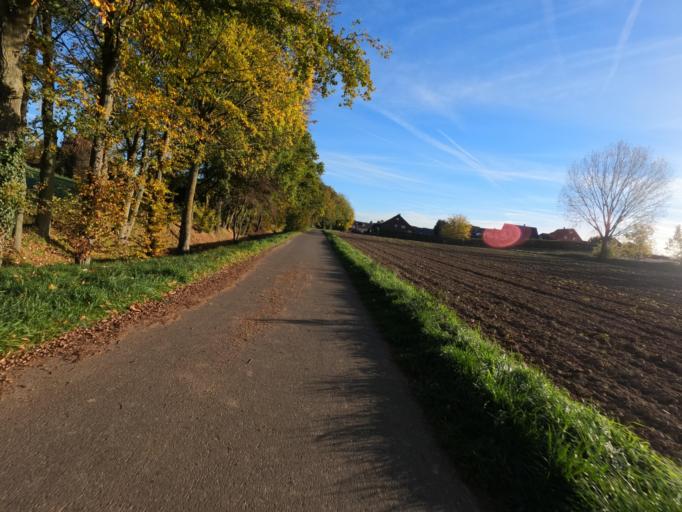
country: DE
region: North Rhine-Westphalia
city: Erkelenz
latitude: 51.0318
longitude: 6.3519
